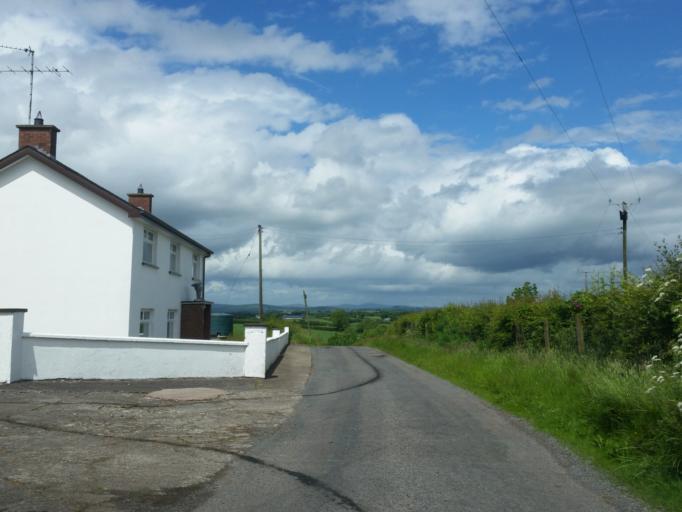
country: GB
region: Northern Ireland
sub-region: Omagh District
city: Omagh
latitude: 54.5417
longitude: -7.1347
